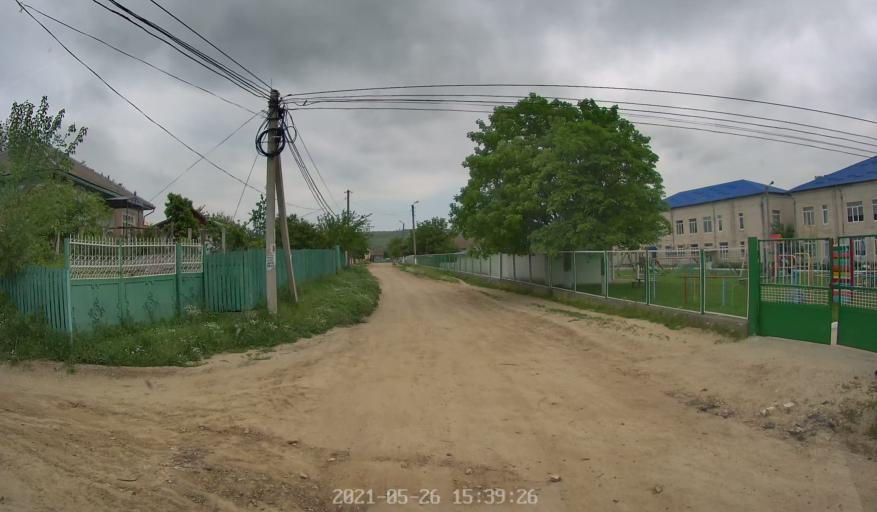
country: MD
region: Hincesti
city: Dancu
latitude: 46.6674
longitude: 28.3216
